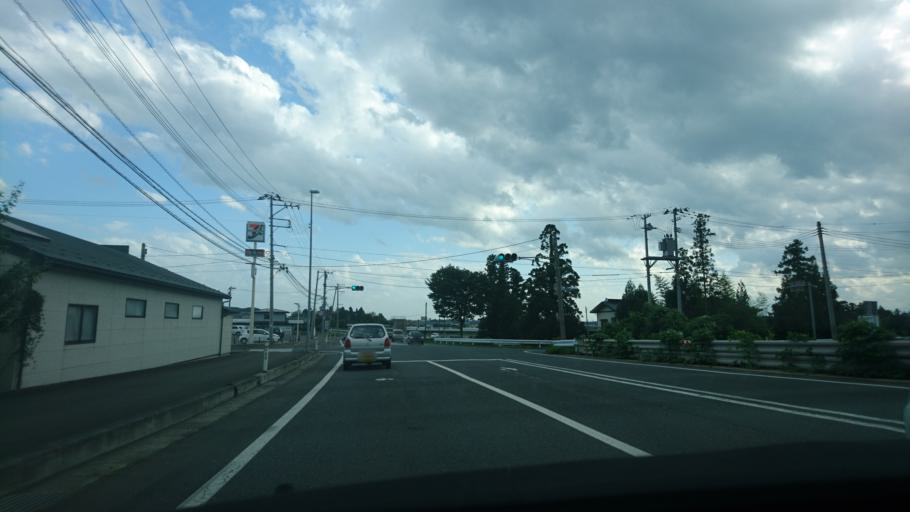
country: JP
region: Iwate
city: Kitakami
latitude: 39.2514
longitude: 141.1200
